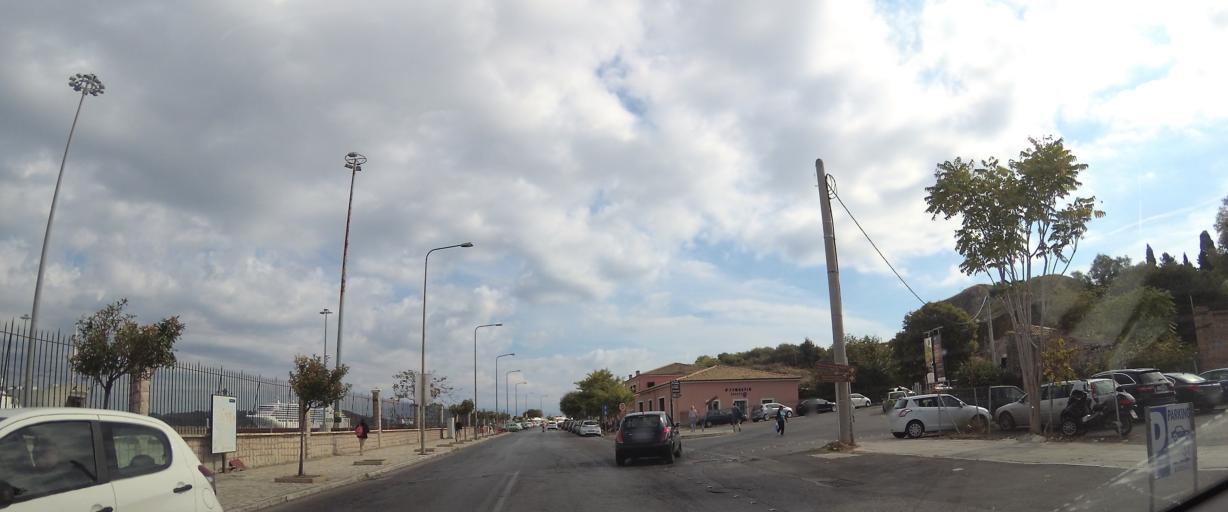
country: GR
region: Ionian Islands
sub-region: Nomos Kerkyras
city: Kerkyra
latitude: 39.6265
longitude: 19.9132
